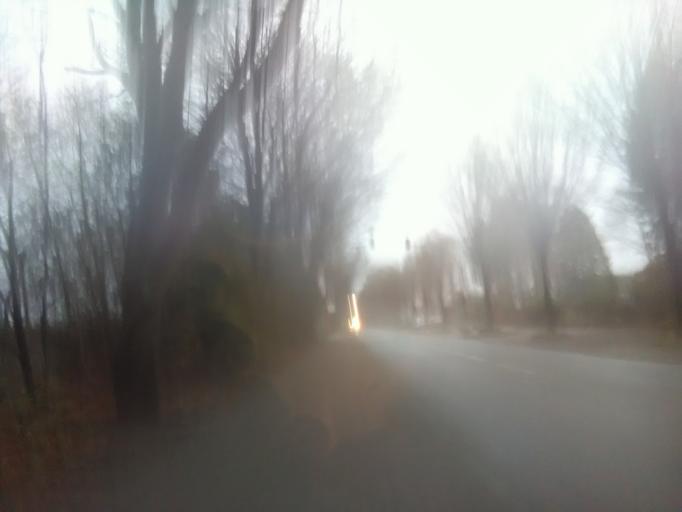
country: DE
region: Schleswig-Holstein
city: Quickborn
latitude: 53.7251
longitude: 9.9341
